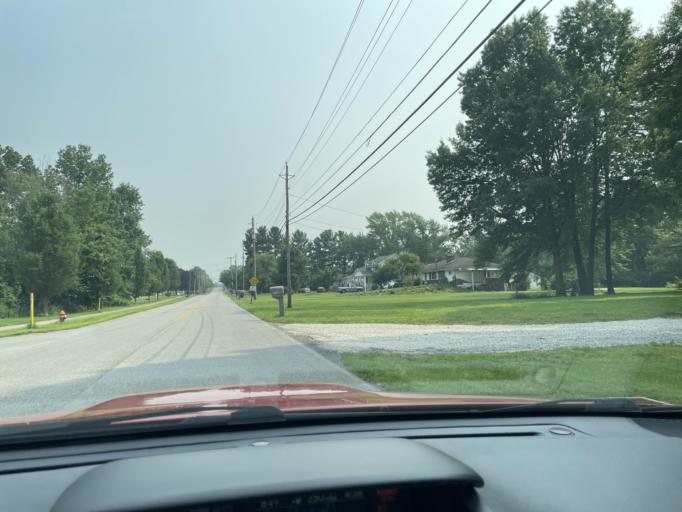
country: US
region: Ohio
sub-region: Trumbull County
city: McDonald
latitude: 41.1565
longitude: -80.7328
